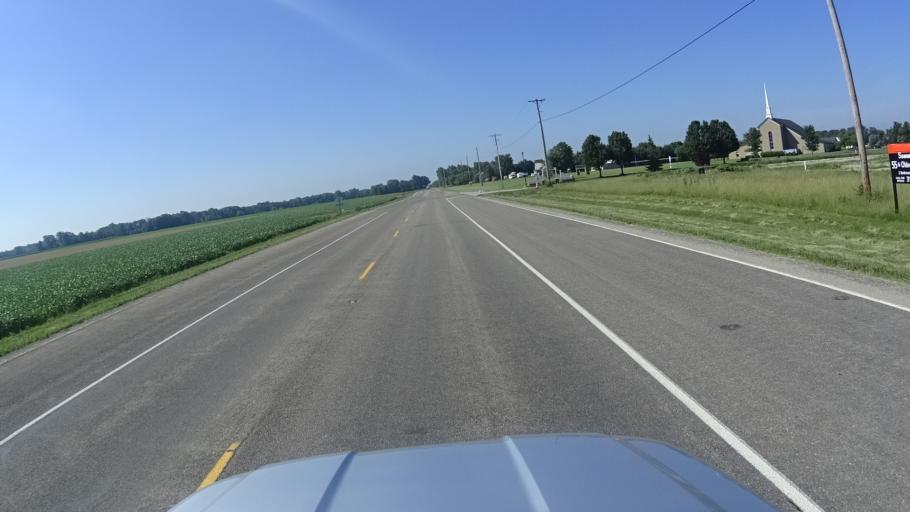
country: US
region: Indiana
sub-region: Madison County
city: Ingalls
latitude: 39.9866
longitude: -85.8432
